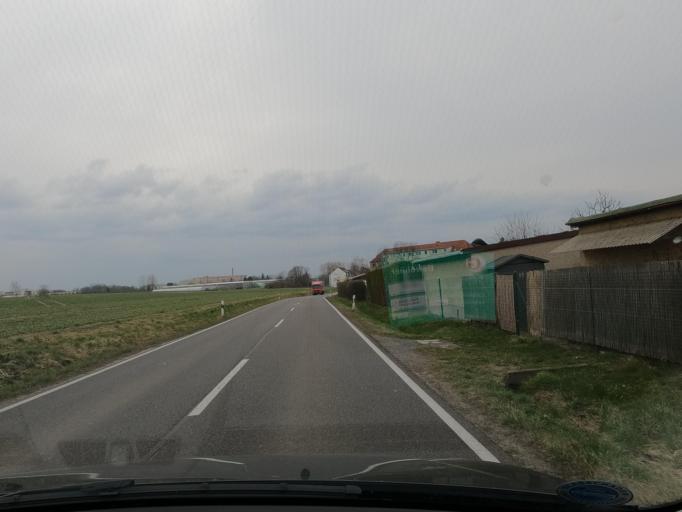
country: DE
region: Saxony
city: Schkeuditz
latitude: 51.4005
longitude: 12.2311
